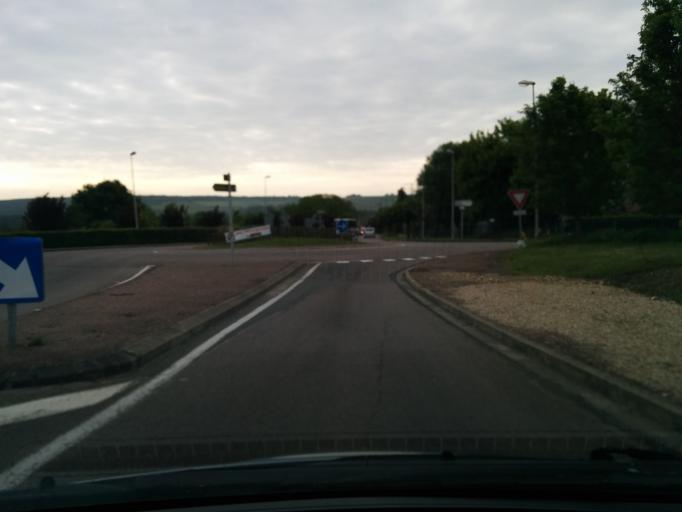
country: FR
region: Haute-Normandie
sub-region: Departement de l'Eure
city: Gasny
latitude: 49.0946
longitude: 1.5948
